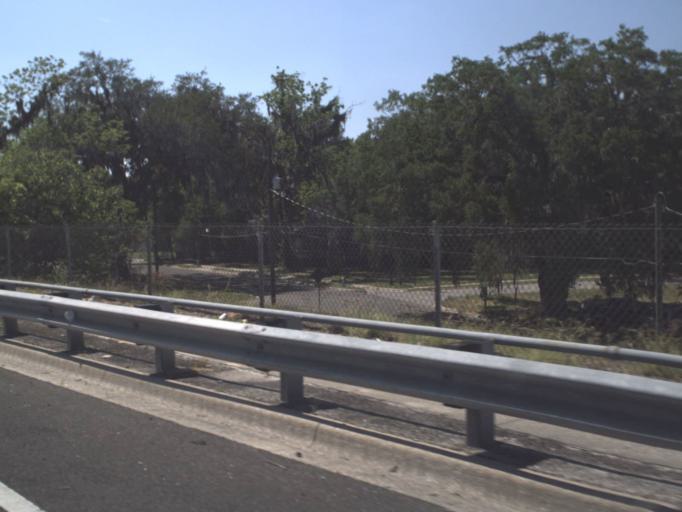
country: US
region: Florida
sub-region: Marion County
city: Ocala
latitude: 29.1869
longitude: -82.1432
